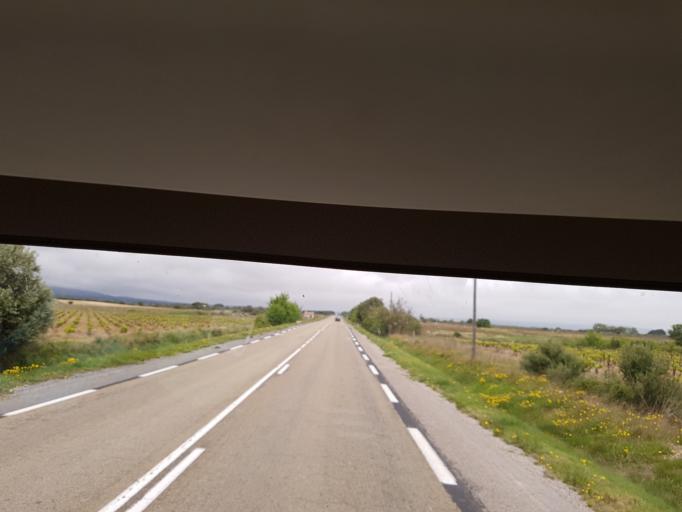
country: FR
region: Languedoc-Roussillon
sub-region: Departement de l'Aude
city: Leucate
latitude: 42.9199
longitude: 2.9962
